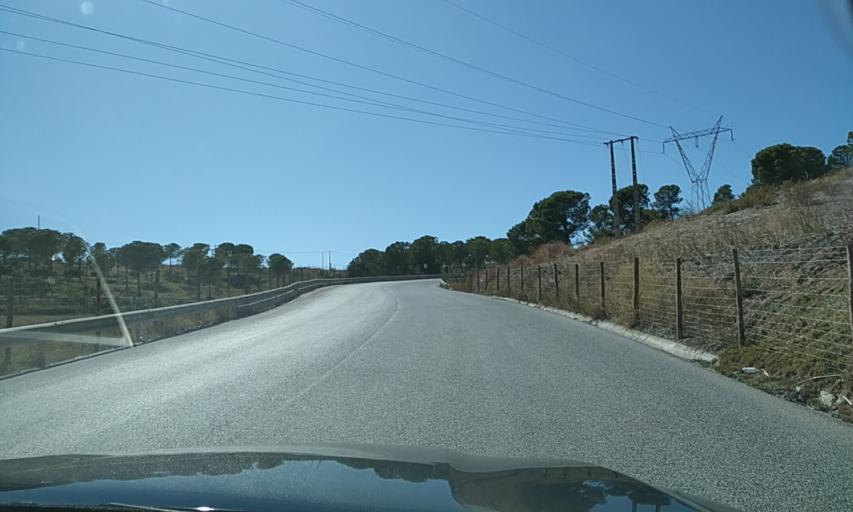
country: PT
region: Lisbon
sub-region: Alenquer
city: Alenquer
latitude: 39.0662
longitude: -9.0023
